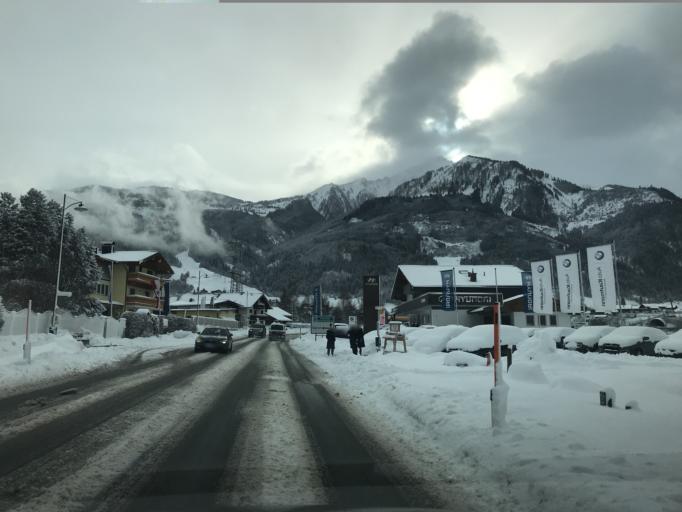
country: AT
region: Salzburg
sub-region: Politischer Bezirk Zell am See
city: Kaprun
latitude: 47.2787
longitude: 12.7567
